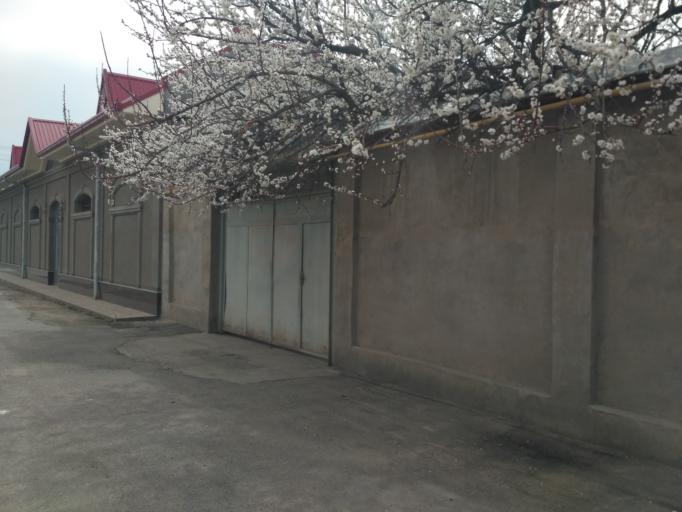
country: UZ
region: Toshkent Shahri
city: Bektemir
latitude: 41.2694
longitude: 69.2977
